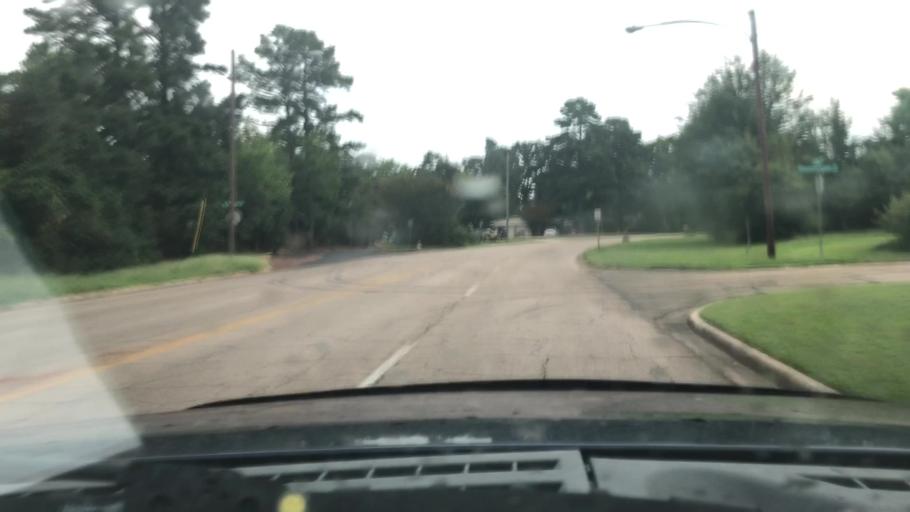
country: US
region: Texas
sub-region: Bowie County
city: Wake Village
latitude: 33.4024
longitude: -94.0802
